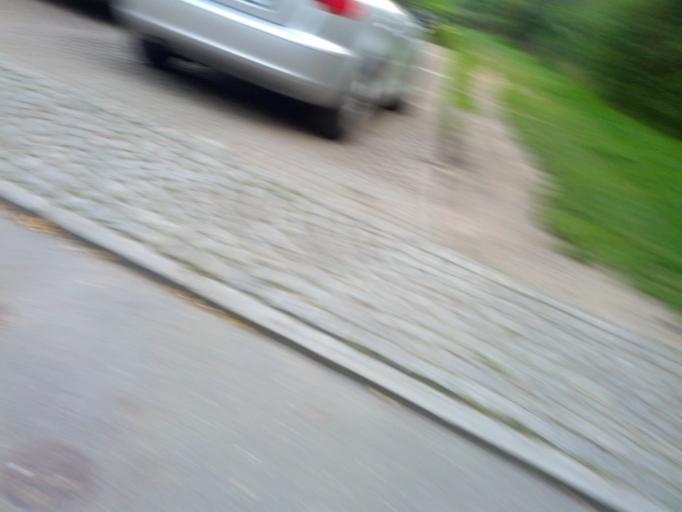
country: DE
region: Mecklenburg-Vorpommern
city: Ostseebad Kuhlungsborn
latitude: 54.1502
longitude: 11.7513
